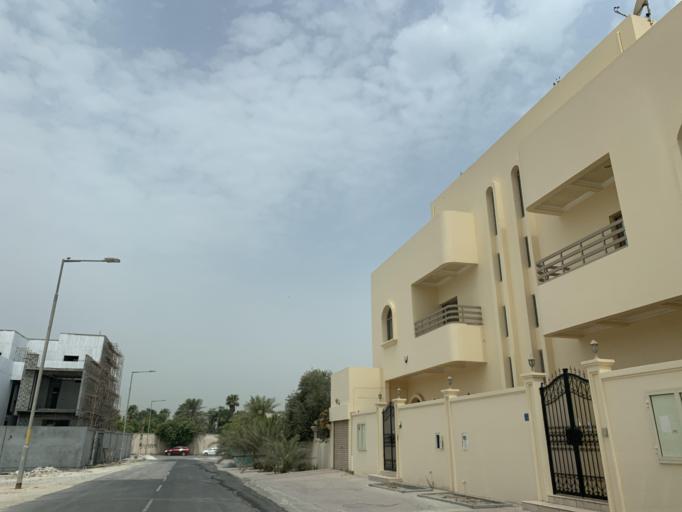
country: BH
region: Central Governorate
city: Madinat Hamad
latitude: 26.1826
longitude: 50.4726
